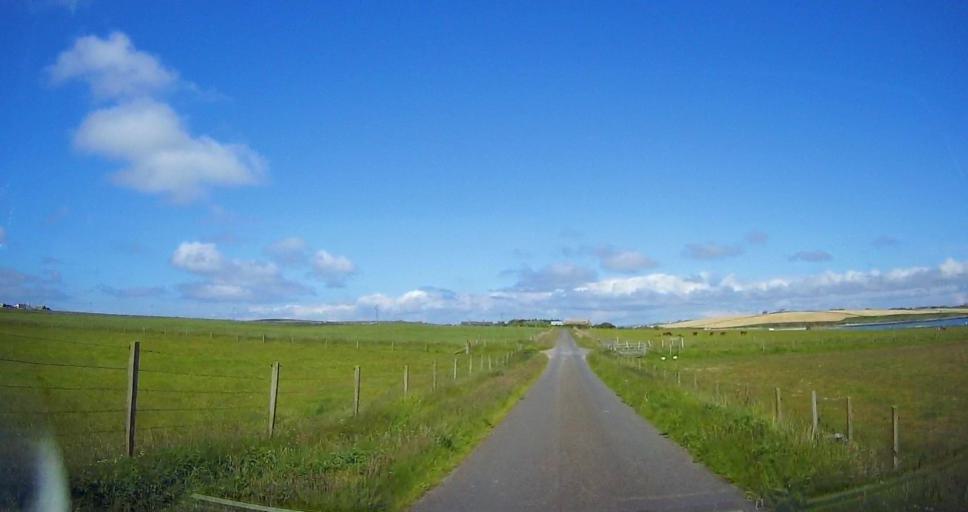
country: GB
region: Scotland
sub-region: Orkney Islands
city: Kirkwall
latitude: 58.8330
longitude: -2.8996
